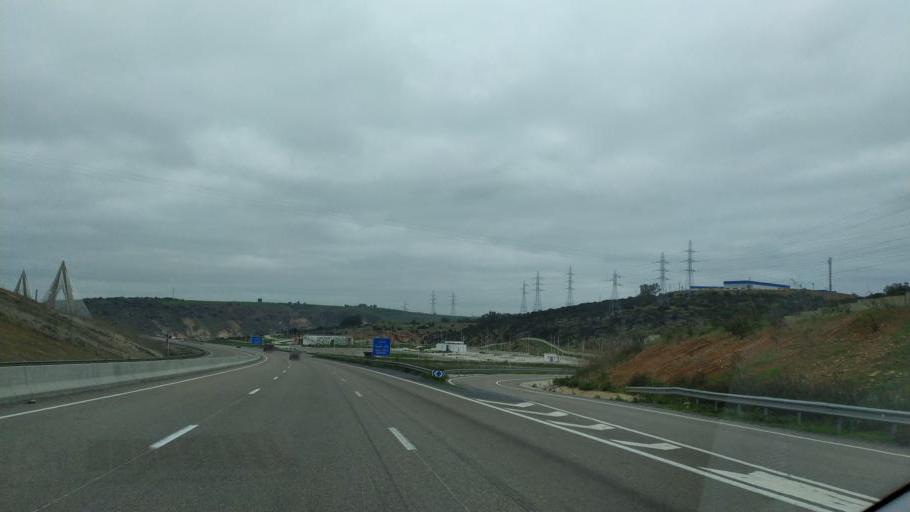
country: MA
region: Rabat-Sale-Zemmour-Zaer
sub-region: Rabat
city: Rabat
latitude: 33.9268
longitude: -6.7631
